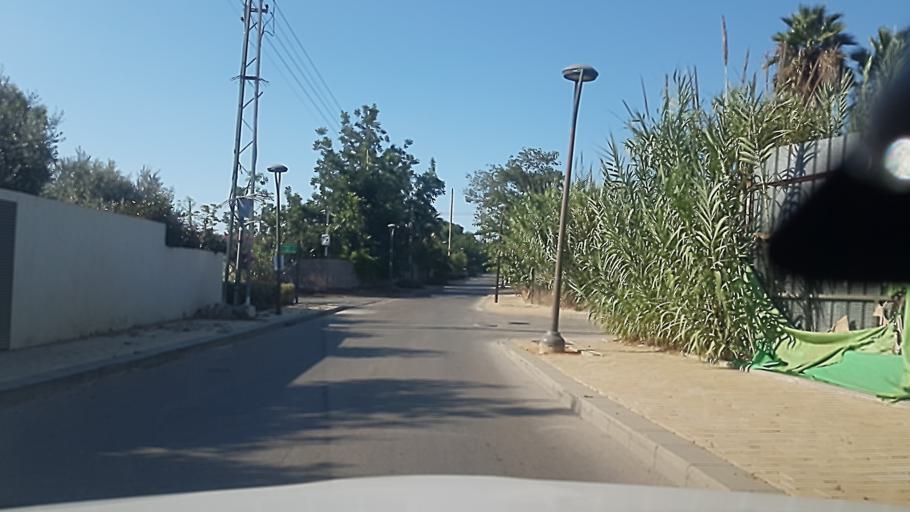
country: IL
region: Tel Aviv
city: Giv`at Shemu'el
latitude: 32.0576
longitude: 34.8425
